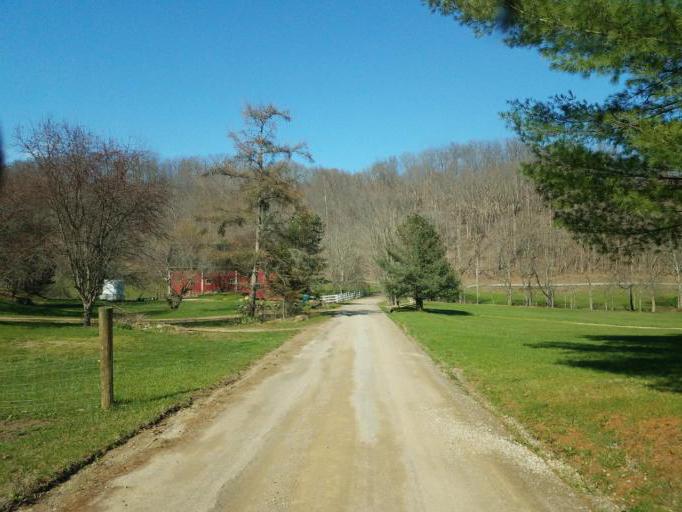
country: US
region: Ohio
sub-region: Knox County
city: Oak Hill
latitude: 40.4329
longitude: -82.2070
